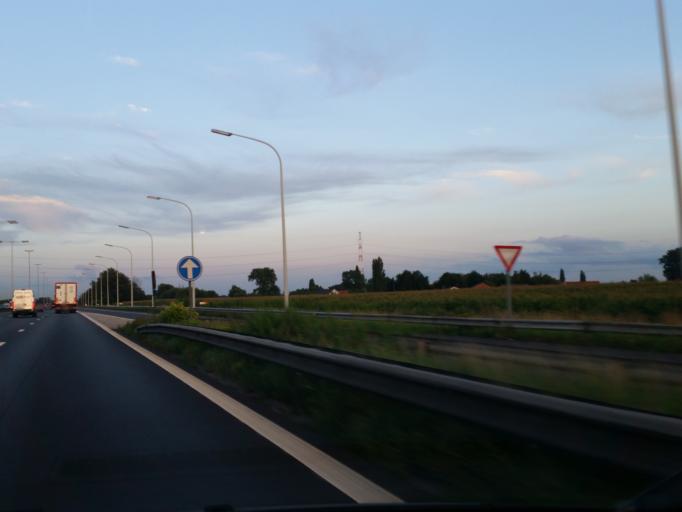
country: BE
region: Flanders
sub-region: Provincie Oost-Vlaanderen
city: Nevele
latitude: 51.0583
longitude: 3.5307
